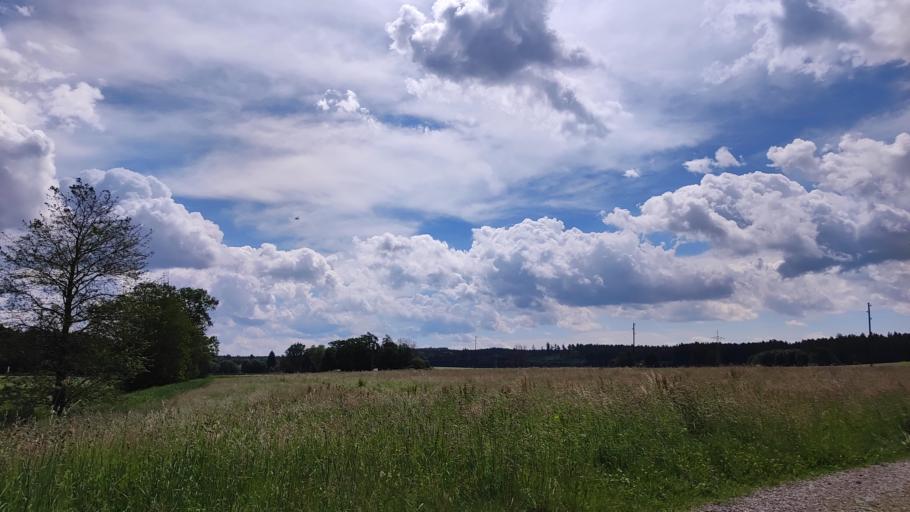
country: DE
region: Bavaria
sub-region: Swabia
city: Horgau
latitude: 48.3899
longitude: 10.6983
